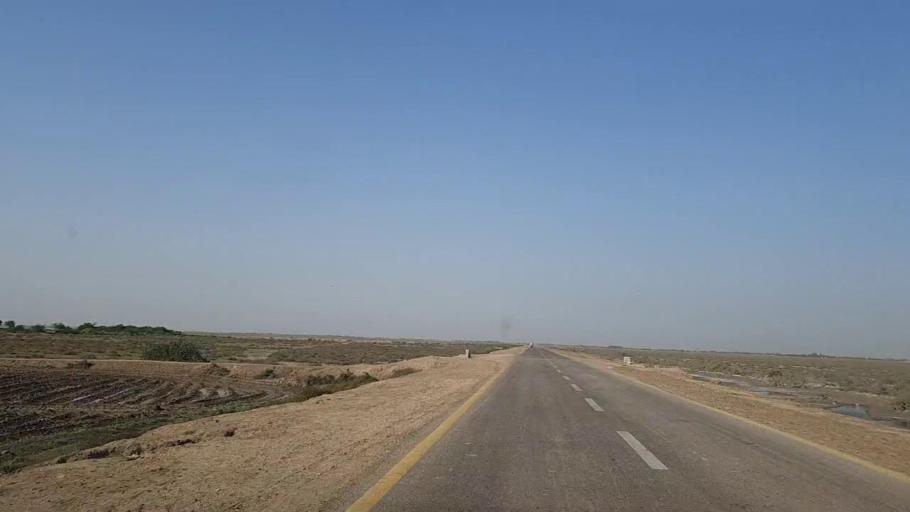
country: PK
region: Sindh
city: Jati
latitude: 24.4859
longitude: 68.3743
